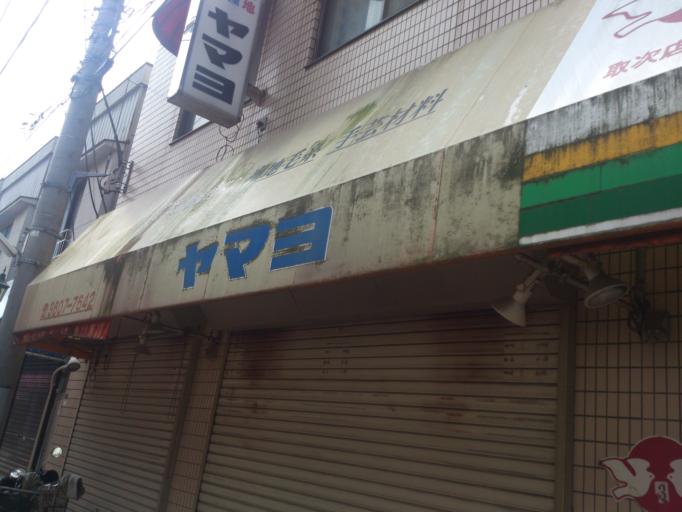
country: JP
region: Chiba
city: Matsudo
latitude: 35.7569
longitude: 139.8749
